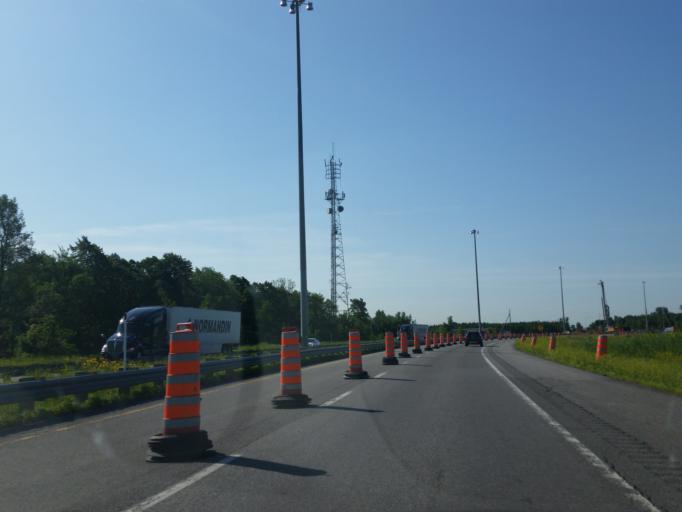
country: CA
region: Quebec
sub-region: Monteregie
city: Napierville
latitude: 45.2698
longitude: -73.4690
